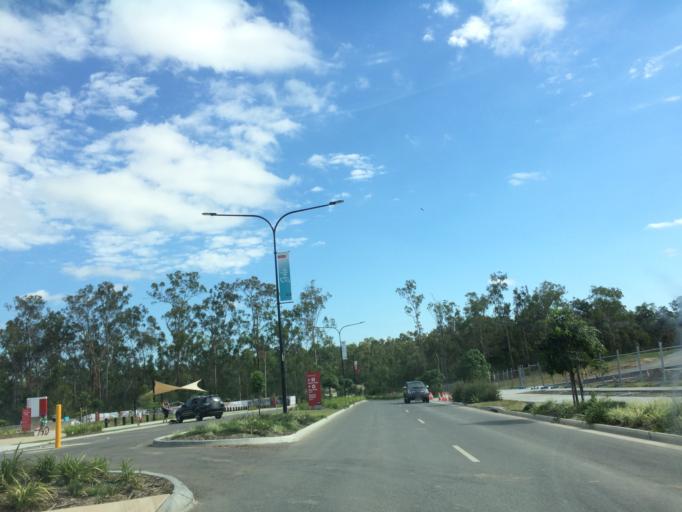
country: AU
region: Queensland
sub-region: Logan
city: North Maclean
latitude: -27.8060
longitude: 152.9462
